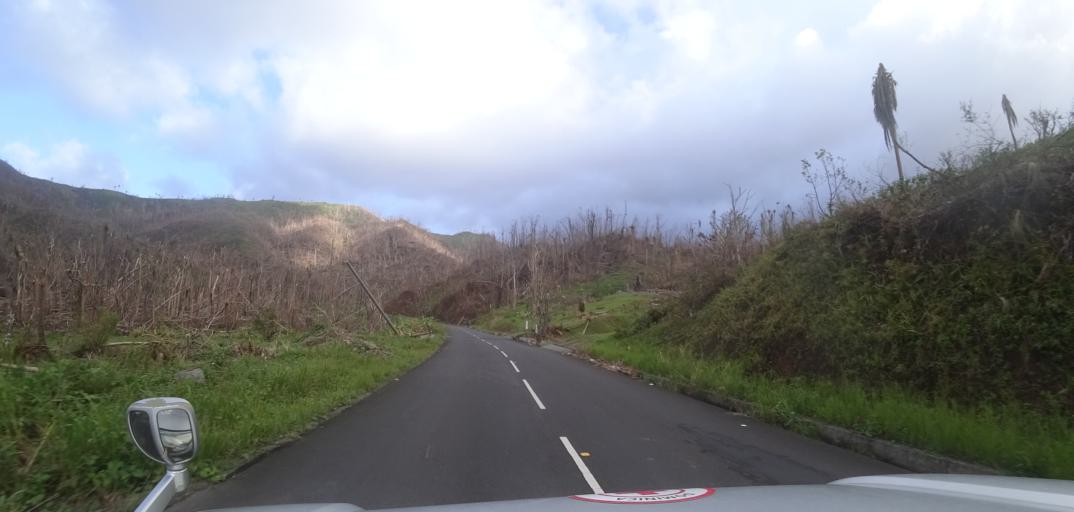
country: DM
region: Saint Andrew
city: Marigot
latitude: 15.5029
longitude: -61.2787
